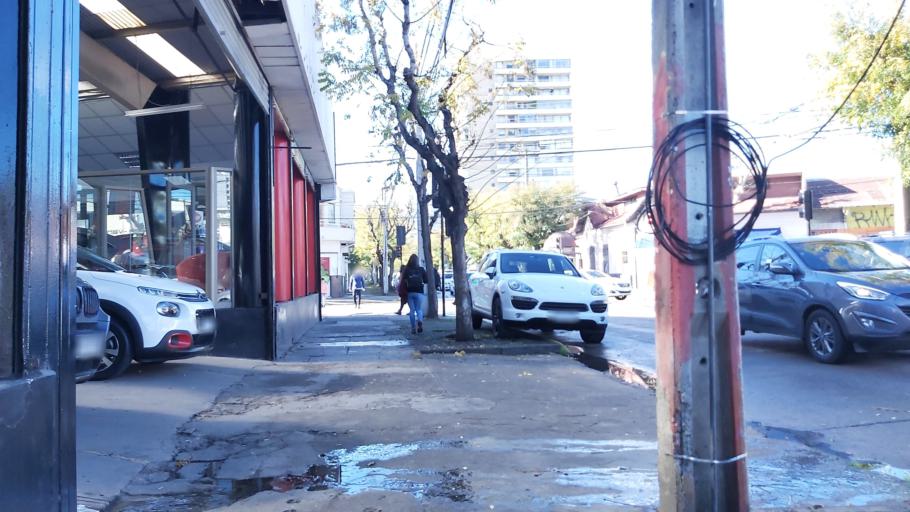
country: CL
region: Valparaiso
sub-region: Provincia de Valparaiso
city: Vina del Mar
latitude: -33.0170
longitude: -71.5460
